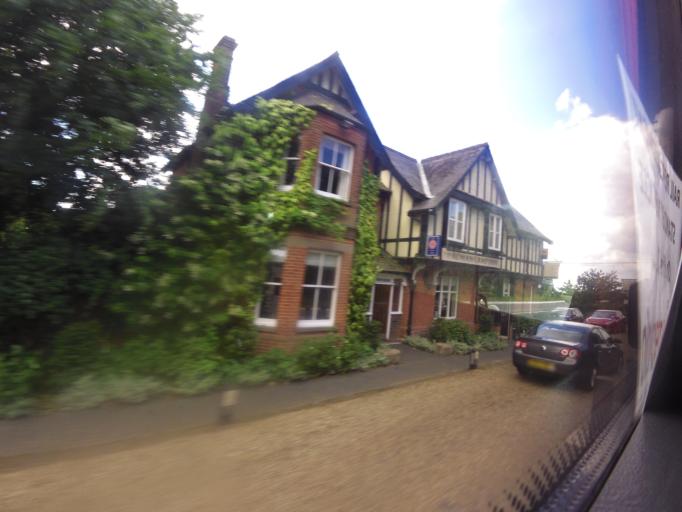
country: GB
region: England
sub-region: Norfolk
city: Sheringham
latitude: 52.9183
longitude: 1.2477
